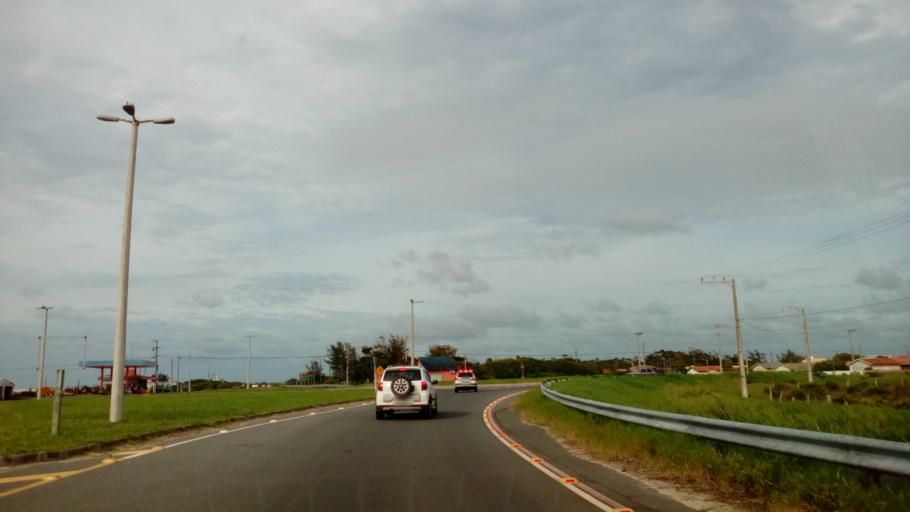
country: BR
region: Santa Catarina
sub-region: Laguna
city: Laguna
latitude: -28.5949
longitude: -48.8395
